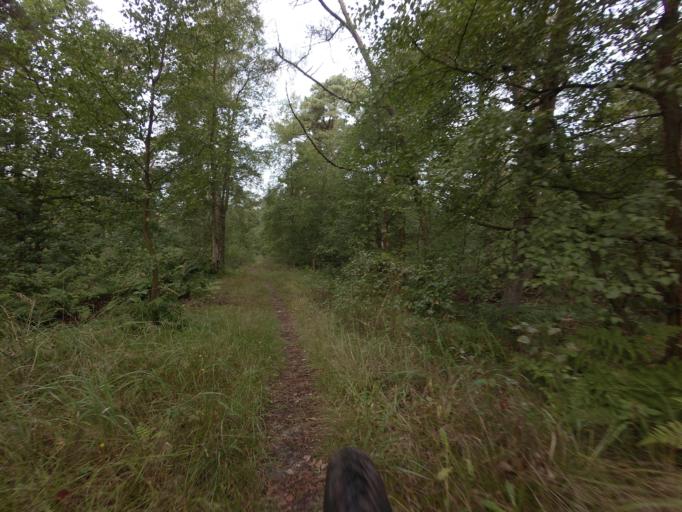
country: DK
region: North Denmark
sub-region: Hjorring Kommune
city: Hirtshals
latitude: 57.5791
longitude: 10.0450
